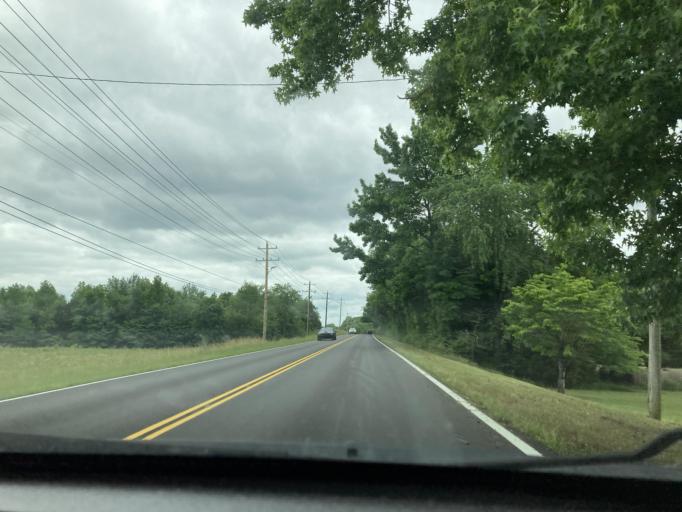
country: US
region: Tennessee
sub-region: Dickson County
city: Burns
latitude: 36.0539
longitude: -87.3463
